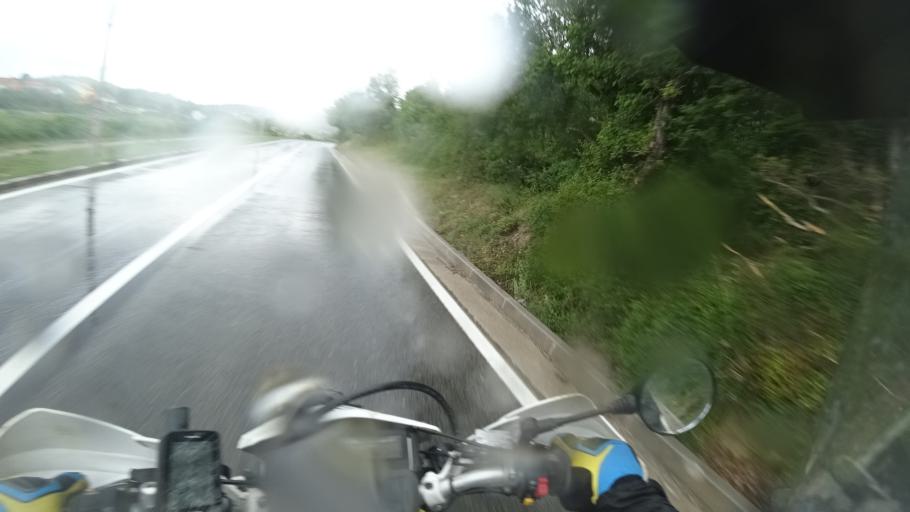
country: HR
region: Sibensko-Kniniska
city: Knin
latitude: 44.0429
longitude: 16.2094
